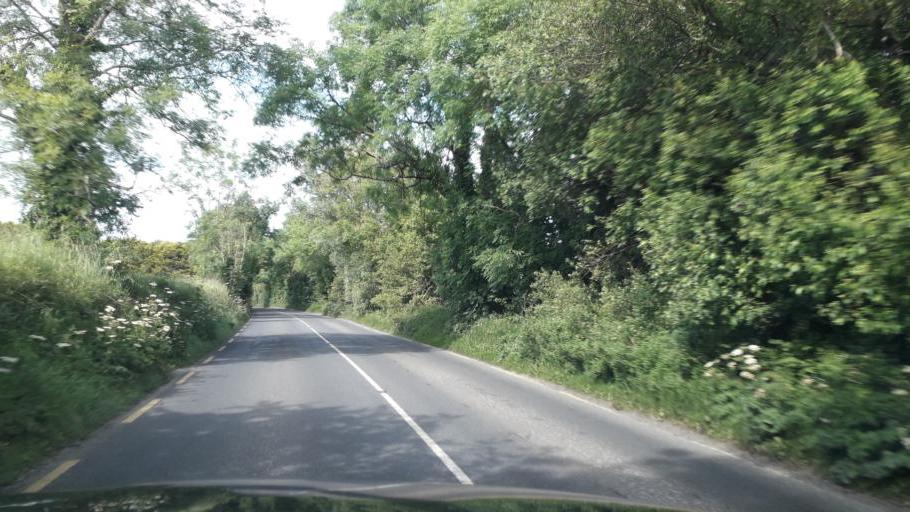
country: IE
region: Leinster
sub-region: Loch Garman
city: Castlebridge
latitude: 52.4119
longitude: -6.4227
